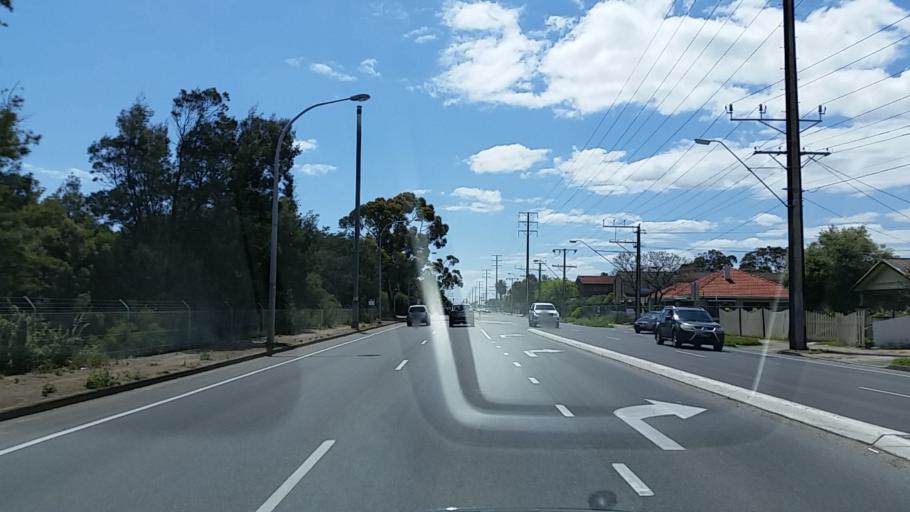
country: AU
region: South Australia
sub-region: Charles Sturt
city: Seaton
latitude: -34.8966
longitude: 138.5140
